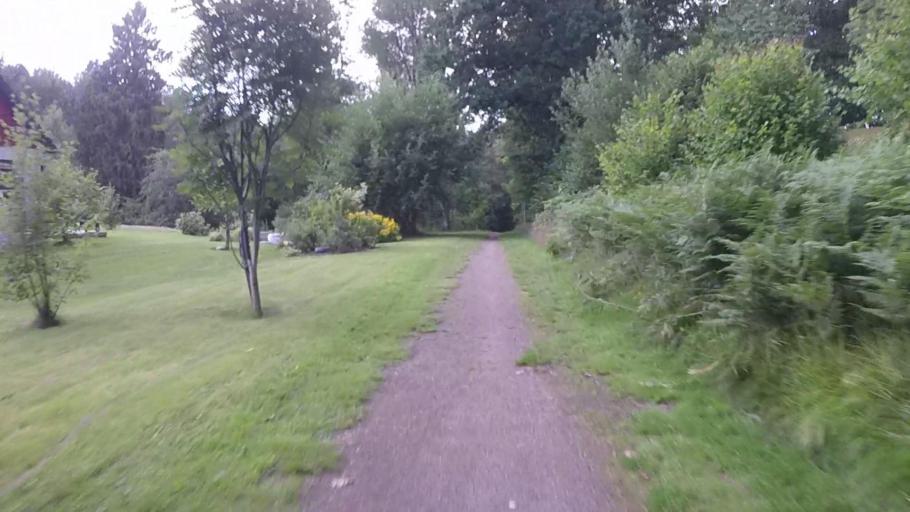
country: SE
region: Vaestra Goetaland
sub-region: Trollhattan
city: Trollhattan
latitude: 58.2553
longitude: 12.2651
